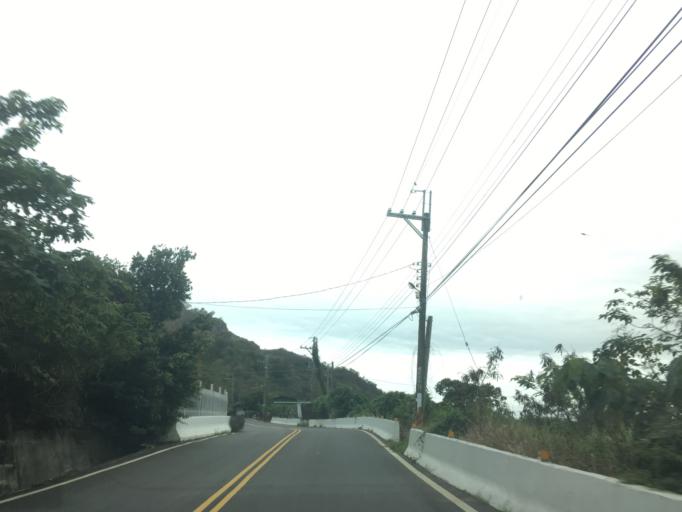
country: TW
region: Taiwan
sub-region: Taitung
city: Taitung
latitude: 22.8176
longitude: 121.1367
